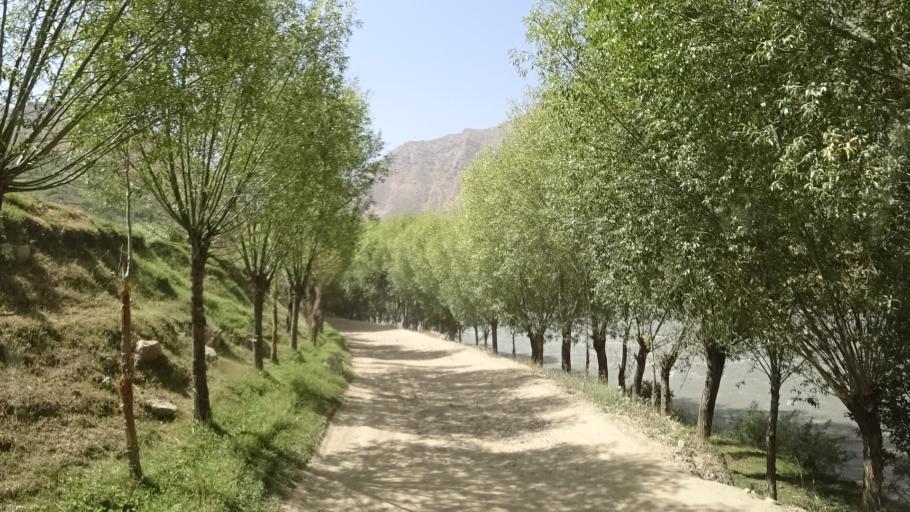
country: TJ
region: Gorno-Badakhshan
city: Khorugh
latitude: 37.1810
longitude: 71.4510
